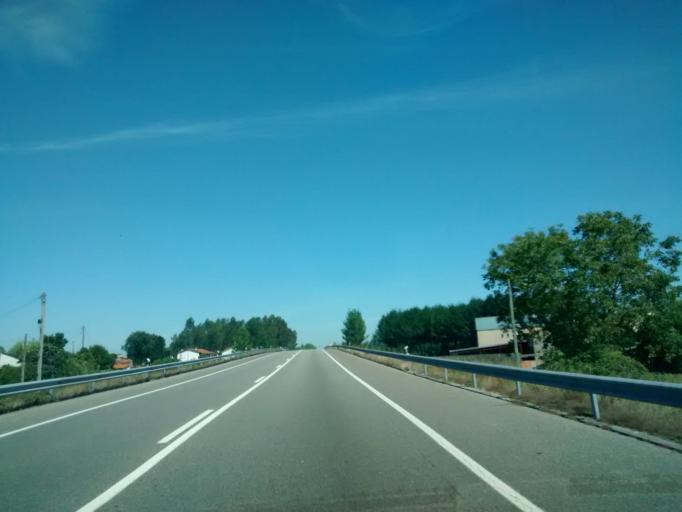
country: PT
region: Aveiro
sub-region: Anadia
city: Sangalhos
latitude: 40.4734
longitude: -8.4715
